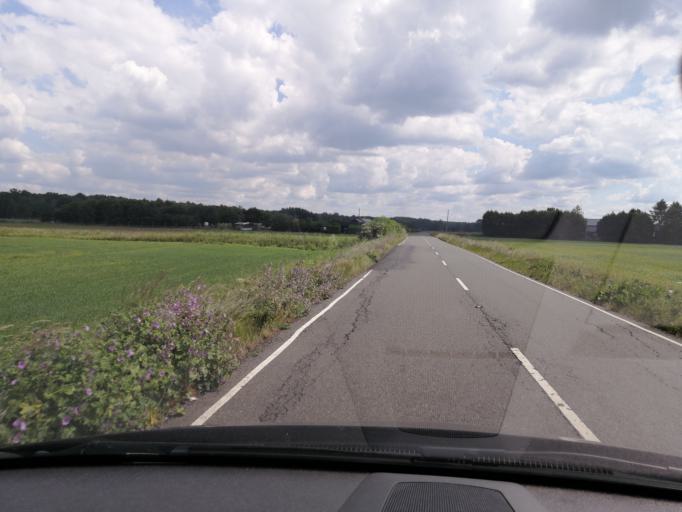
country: GB
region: England
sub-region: Cambridgeshire
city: Yaxley
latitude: 52.4949
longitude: -0.2449
